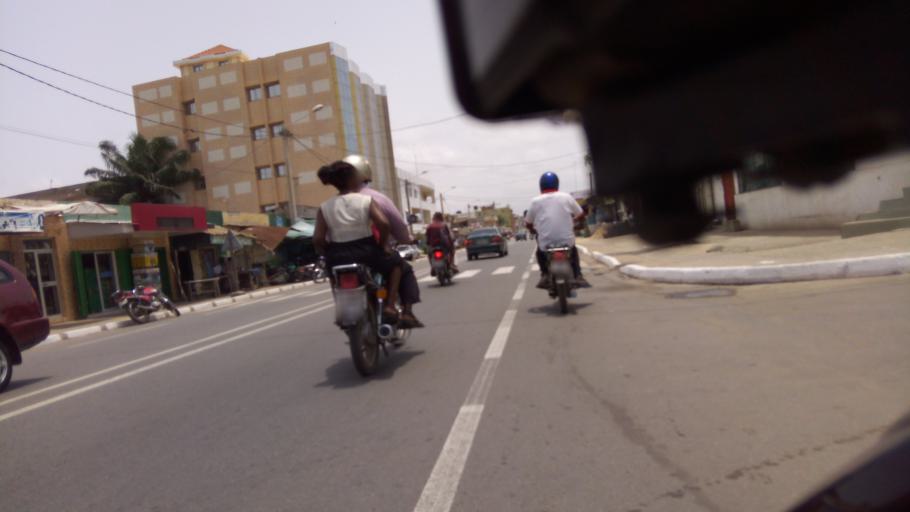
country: TG
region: Maritime
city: Lome
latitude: 6.1463
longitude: 1.2194
